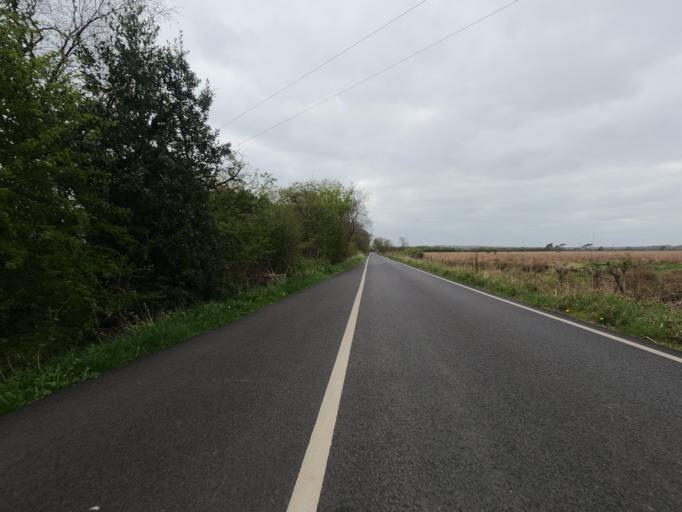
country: GB
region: England
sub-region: Newcastle upon Tyne
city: Dinnington
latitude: 55.0591
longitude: -1.6851
